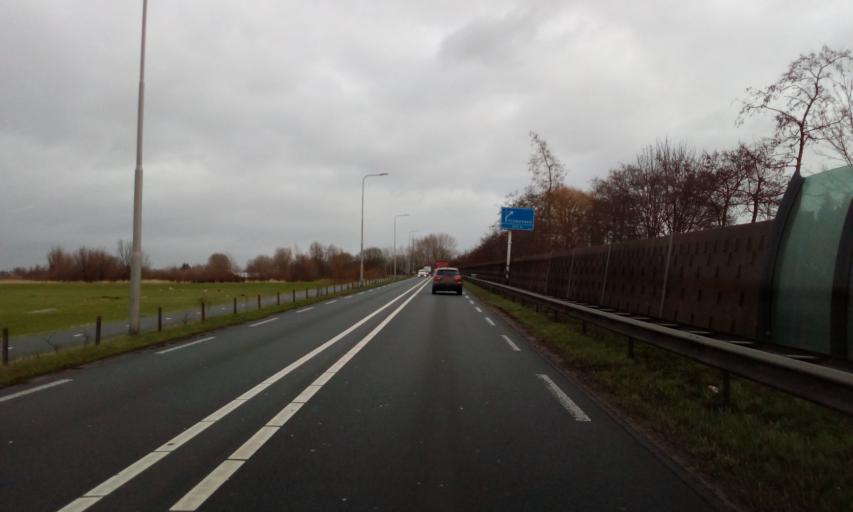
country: NL
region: Utrecht
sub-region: Gemeente De Ronde Venen
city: Mijdrecht
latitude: 52.2162
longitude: 4.9253
